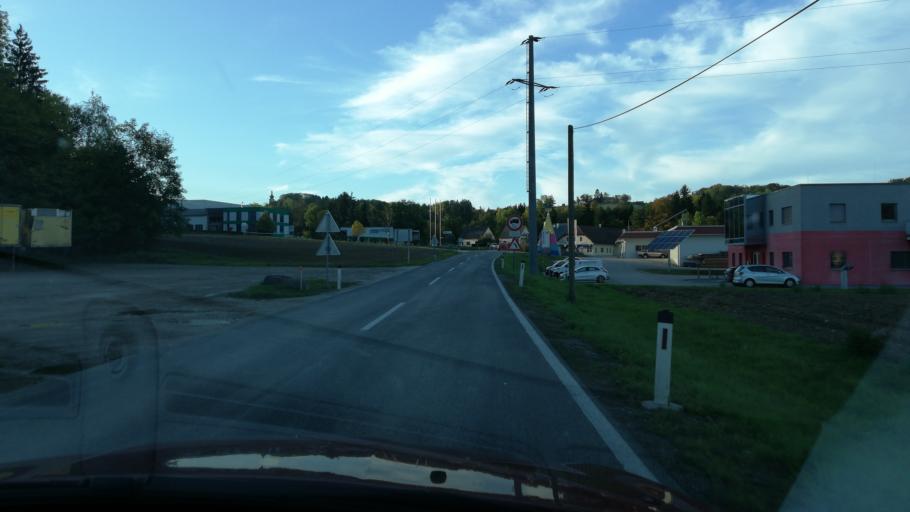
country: AT
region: Upper Austria
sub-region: Politischer Bezirk Steyr-Land
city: Waldneukirchen
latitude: 47.9907
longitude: 14.2754
